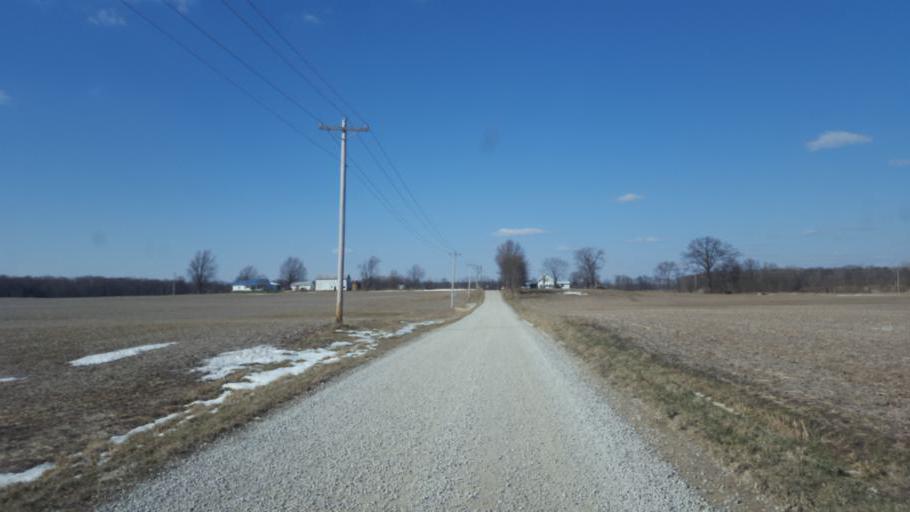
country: US
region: Ohio
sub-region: Morrow County
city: Mount Gilead
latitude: 40.5127
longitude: -82.7783
